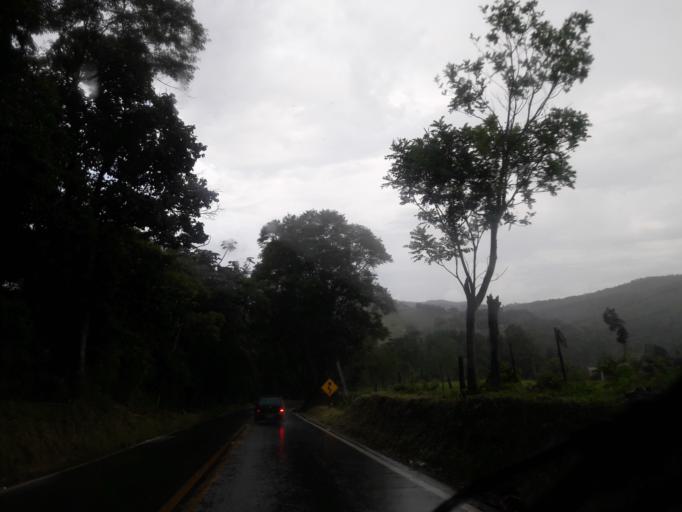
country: BR
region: Sao Paulo
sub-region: Aruja
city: Aruja
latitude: -23.3032
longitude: -46.4355
